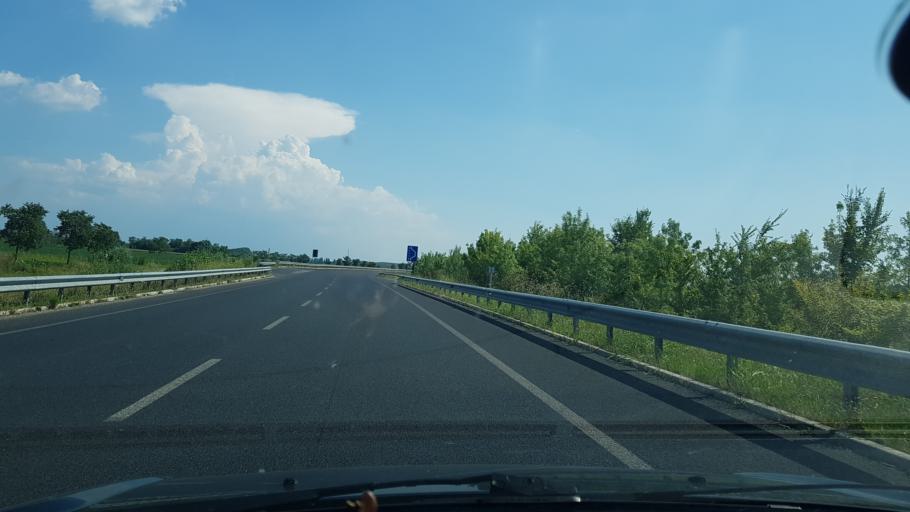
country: IT
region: Friuli Venezia Giulia
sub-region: Provincia di Gorizia
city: Staranzano
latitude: 45.8013
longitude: 13.4884
